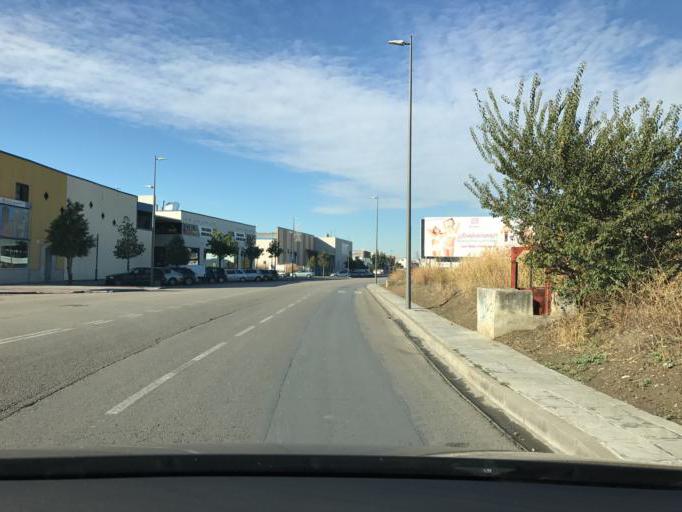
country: ES
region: Andalusia
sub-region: Provincia de Granada
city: Armilla
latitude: 37.1495
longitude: -3.6302
